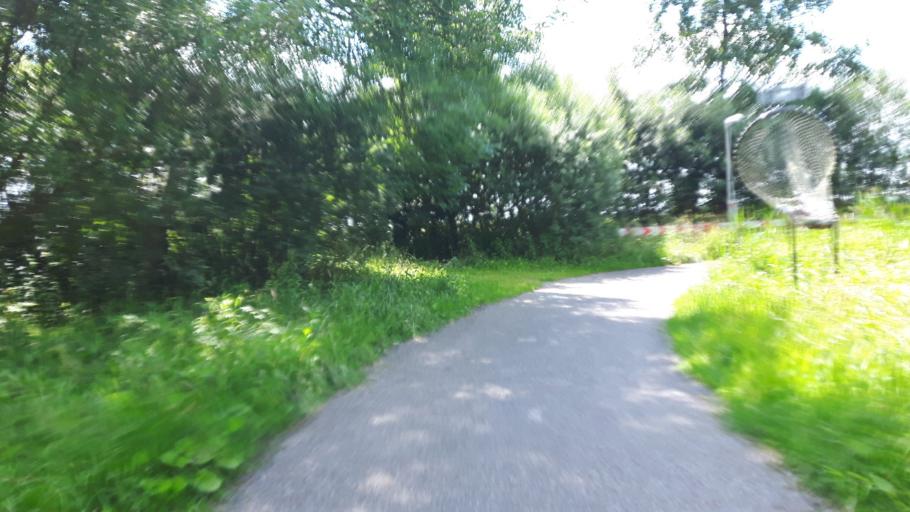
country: NL
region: South Holland
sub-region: Gemeente Vlist
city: Haastrecht
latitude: 52.0393
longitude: 4.7764
